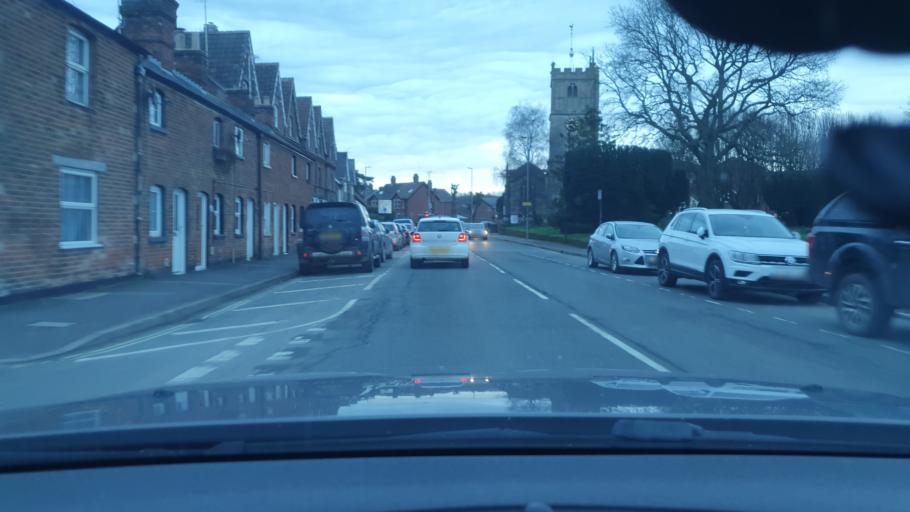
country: GB
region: England
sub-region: Wiltshire
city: Devizes
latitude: 51.3525
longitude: -1.9873
